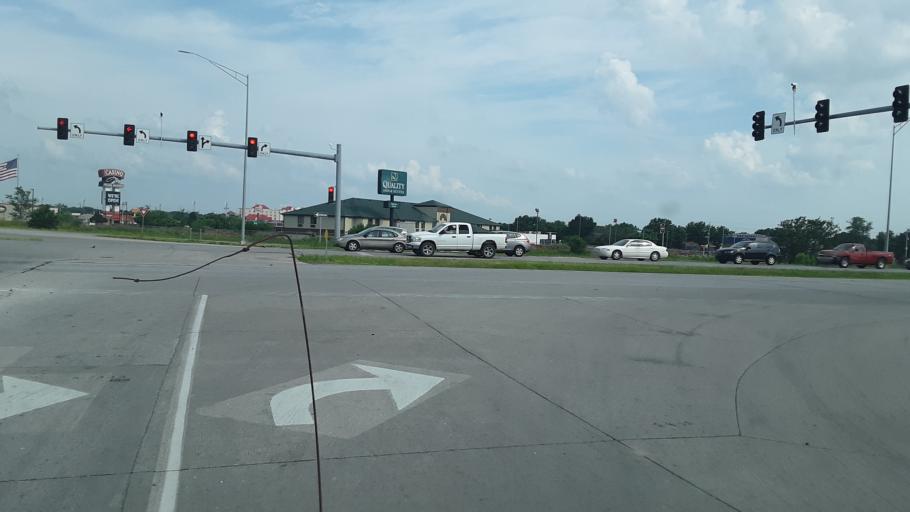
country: US
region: Iowa
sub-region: Polk County
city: Altoona
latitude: 41.6610
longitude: -93.4963
